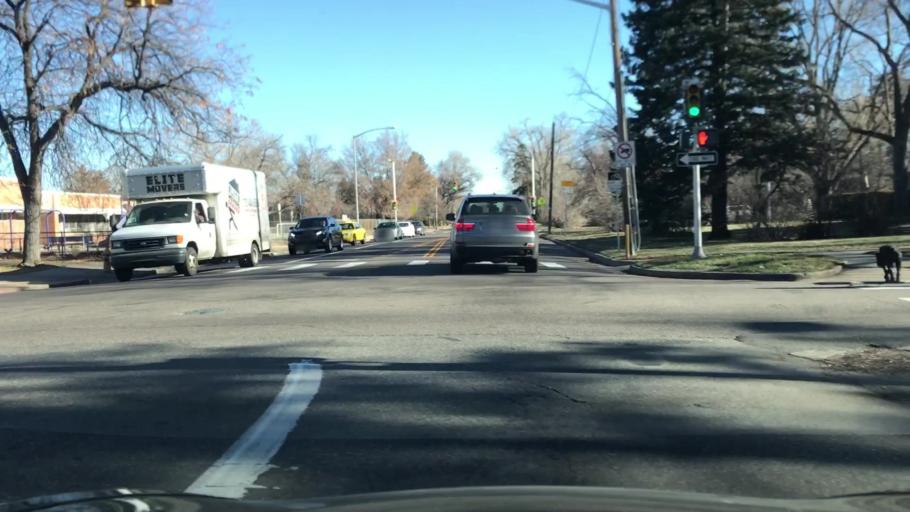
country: US
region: Colorado
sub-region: Arapahoe County
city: Glendale
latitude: 39.7474
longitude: -104.9125
